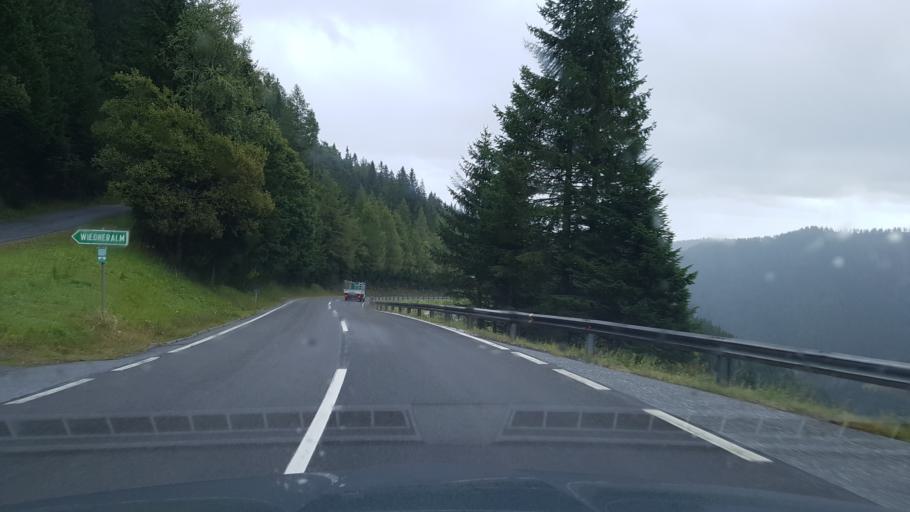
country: AT
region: Styria
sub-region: Politischer Bezirk Voitsberg
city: Salla
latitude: 47.1145
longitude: 14.9291
